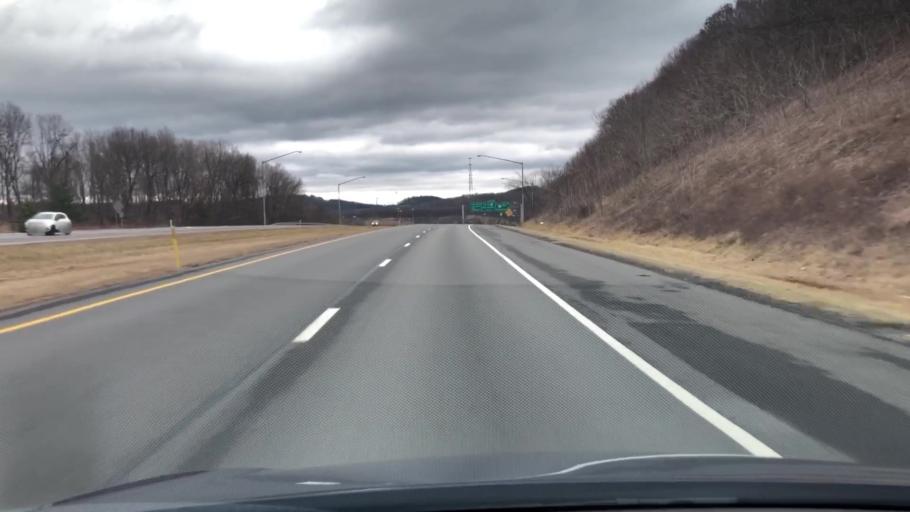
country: US
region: Pennsylvania
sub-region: Westmoreland County
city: New Stanton
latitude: 40.2166
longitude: -79.5915
